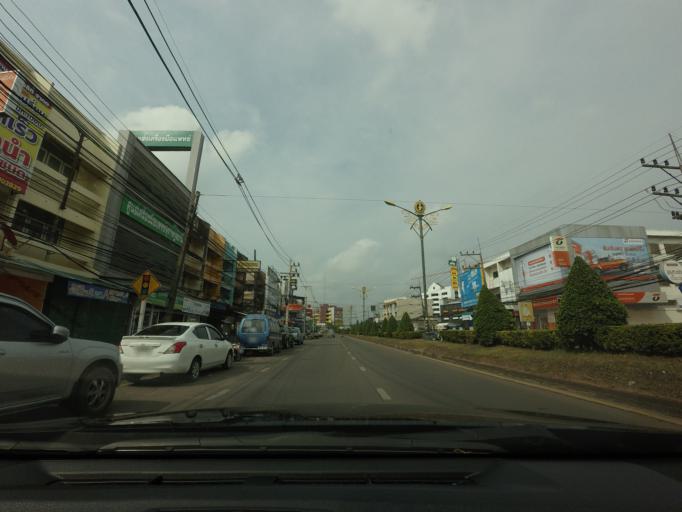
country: TH
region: Surat Thani
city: Surat Thani
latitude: 9.1253
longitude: 99.3120
